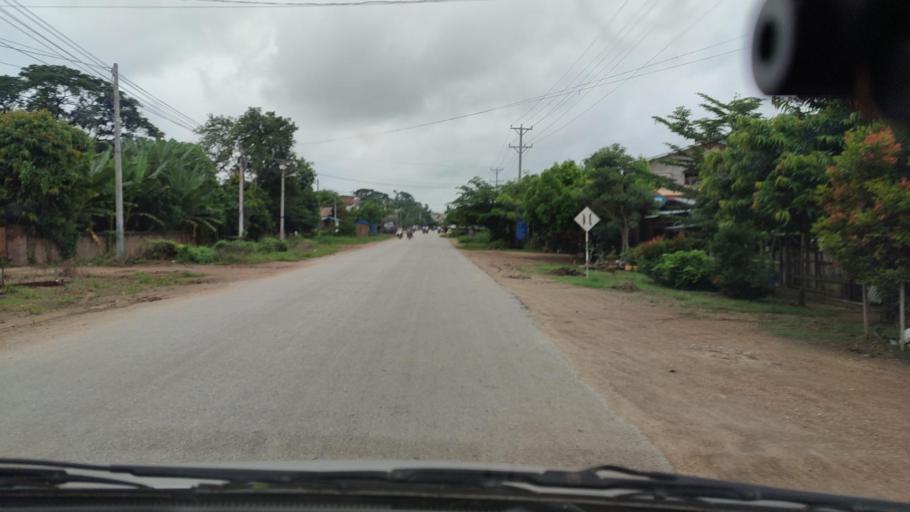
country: MM
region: Bago
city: Pyay
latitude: 18.8520
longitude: 95.3909
